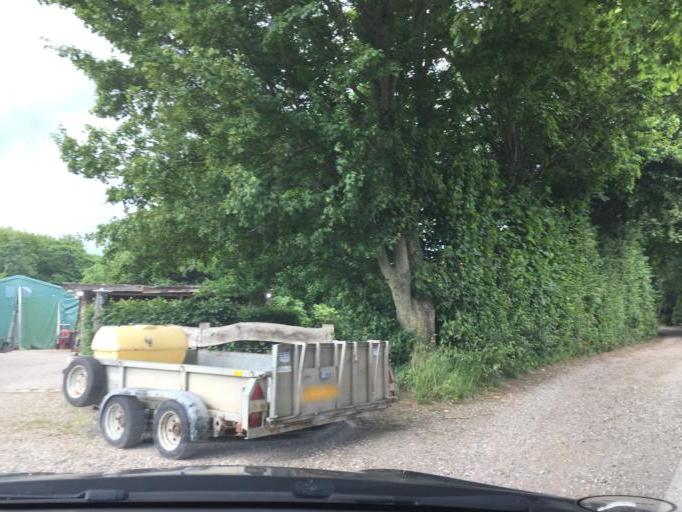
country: DK
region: South Denmark
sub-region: Odense Kommune
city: Neder Holluf
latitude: 55.3507
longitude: 10.5115
